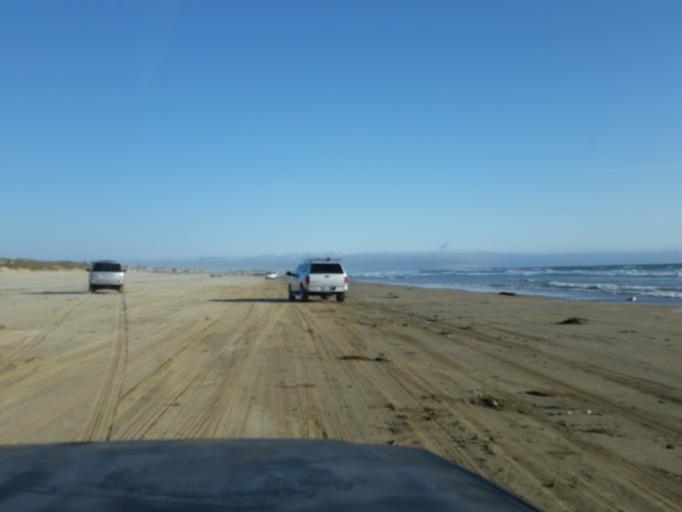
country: US
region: California
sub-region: San Luis Obispo County
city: Grover Beach
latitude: 35.1108
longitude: -120.6330
